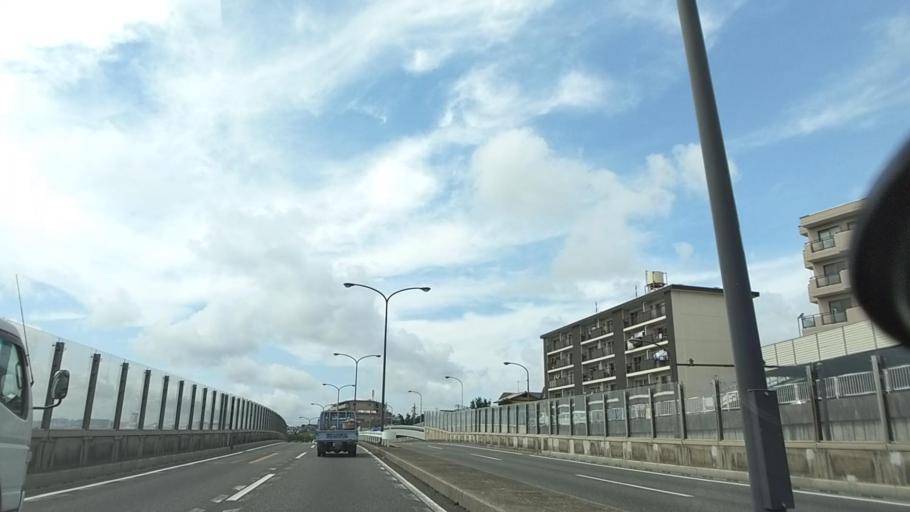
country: JP
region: Kanagawa
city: Yokohama
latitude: 35.4176
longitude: 139.5596
